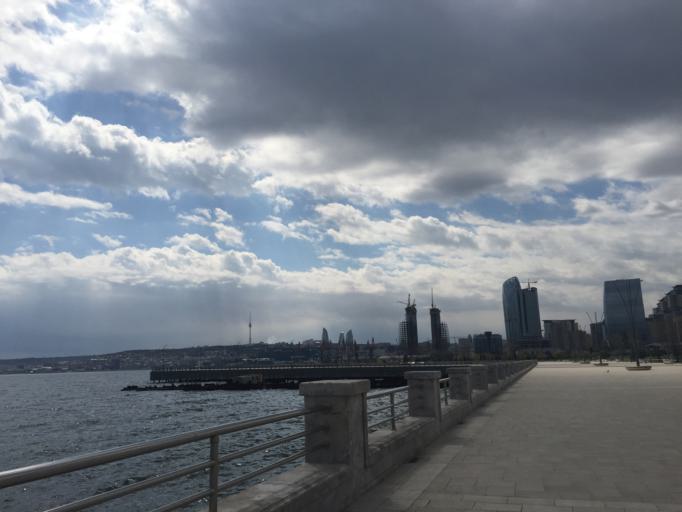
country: AZ
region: Baki
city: Baku
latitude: 40.3747
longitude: 49.8749
